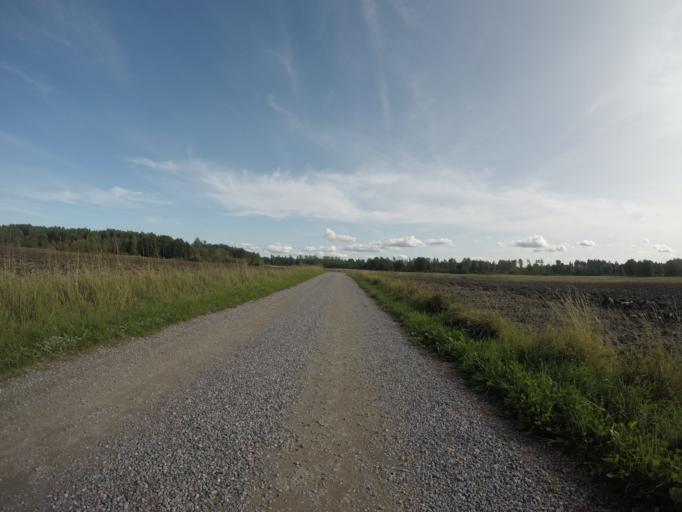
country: SE
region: Soedermanland
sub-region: Eskilstuna Kommun
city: Kvicksund
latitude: 59.5202
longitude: 16.3107
